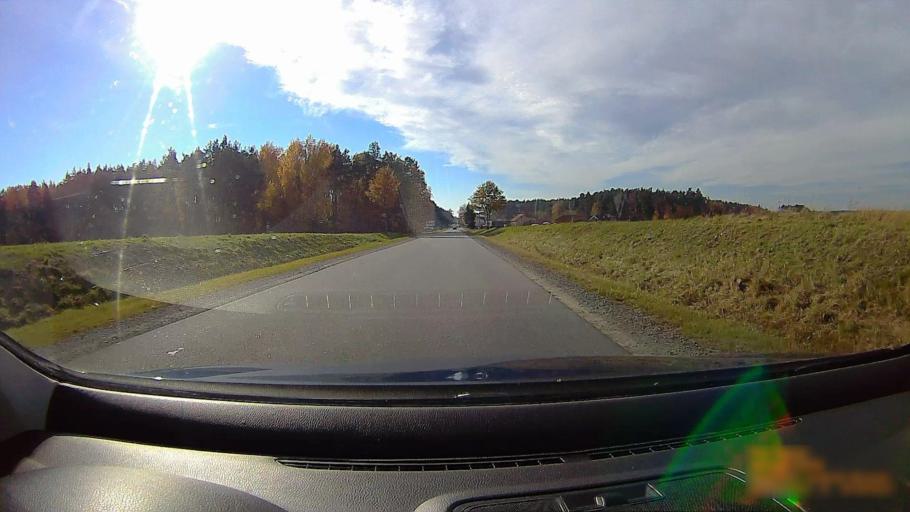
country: PL
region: Greater Poland Voivodeship
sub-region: Powiat ostrzeszowski
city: Doruchow
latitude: 51.3722
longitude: 18.0359
